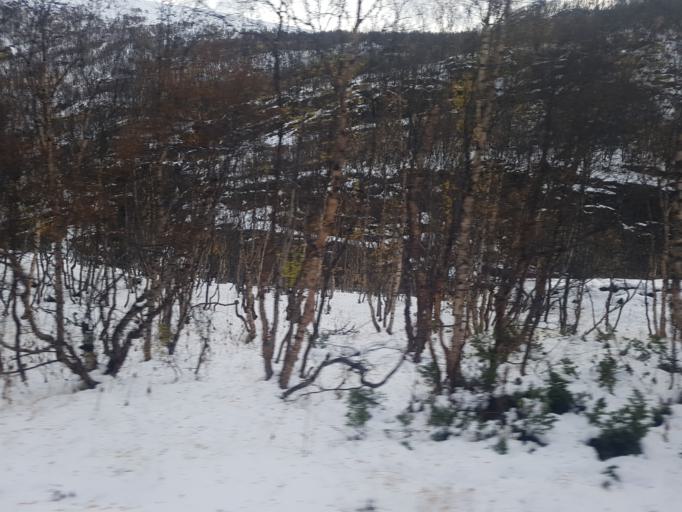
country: NO
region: Sor-Trondelag
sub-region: Oppdal
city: Oppdal
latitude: 62.3358
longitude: 9.6225
